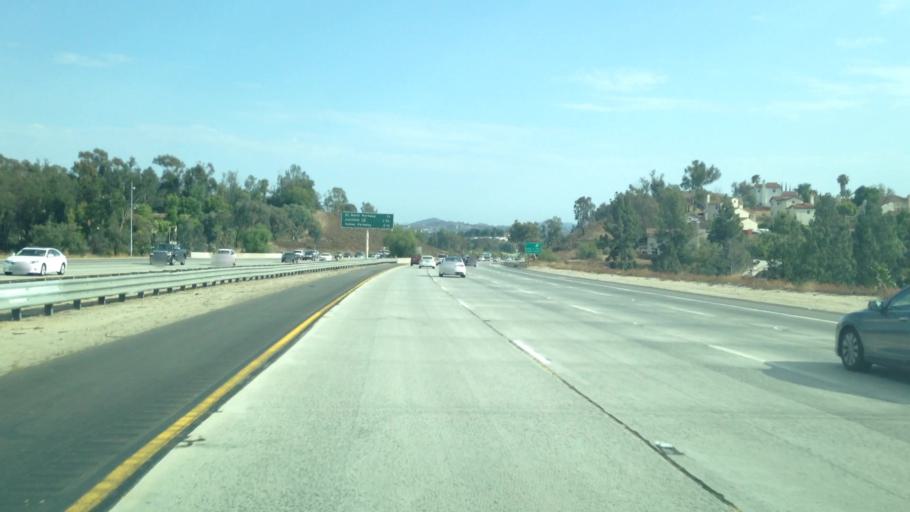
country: US
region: California
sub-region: San Diego County
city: Escondido
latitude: 33.1585
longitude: -117.1046
